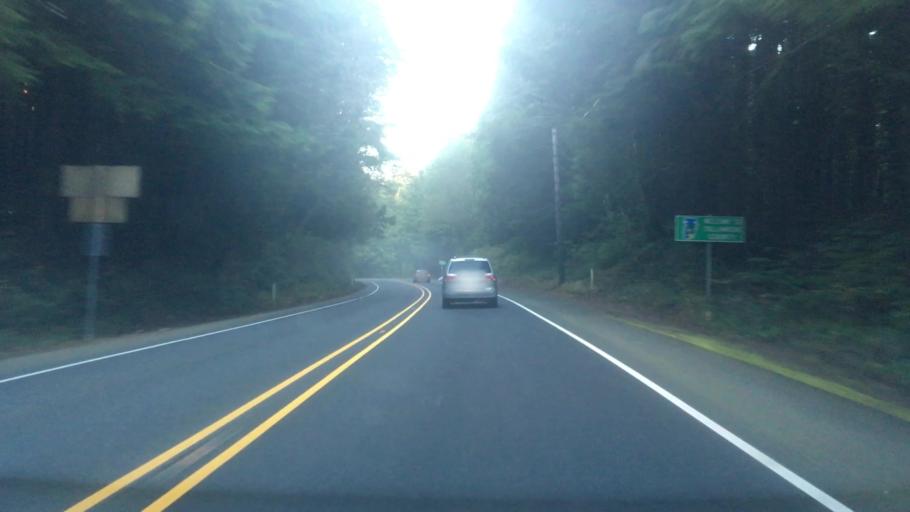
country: US
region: Oregon
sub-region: Clatsop County
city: Cannon Beach
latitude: 45.7831
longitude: -123.9574
